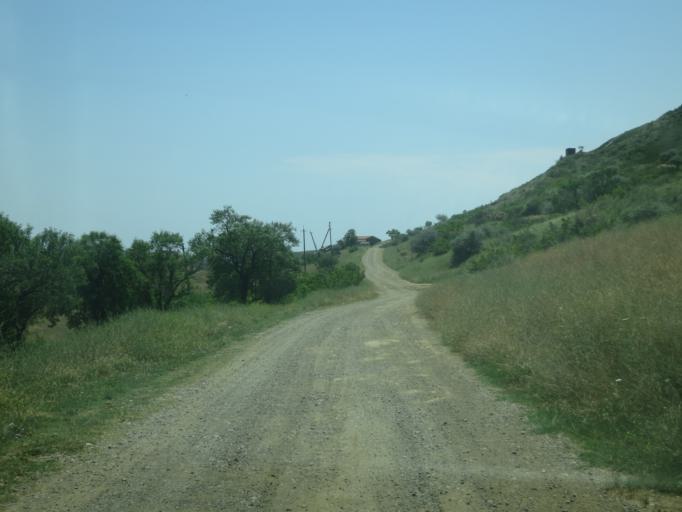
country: AZ
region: Agstafa
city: Saloglu
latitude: 41.4521
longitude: 45.3723
